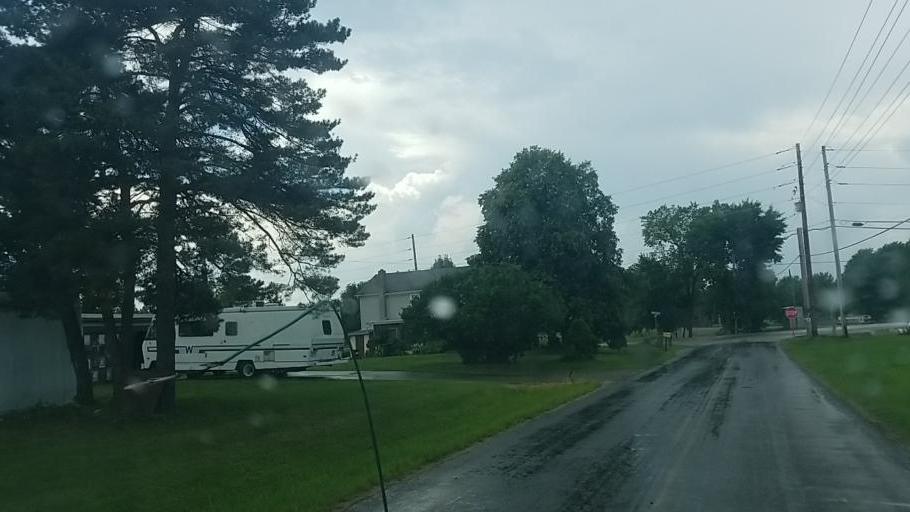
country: US
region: Ohio
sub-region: Lorain County
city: Grafton
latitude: 41.1583
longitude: -82.0223
